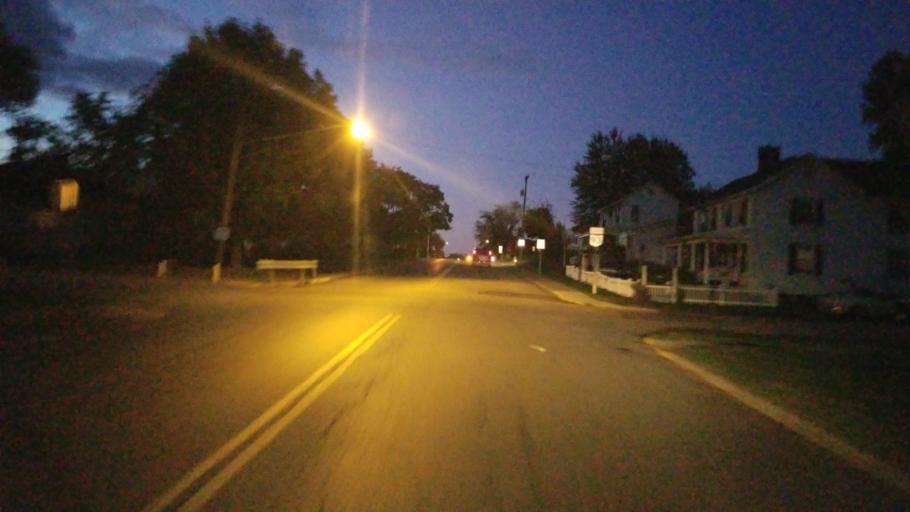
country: US
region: Ohio
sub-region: Vinton County
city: McArthur
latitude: 39.2492
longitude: -82.4787
